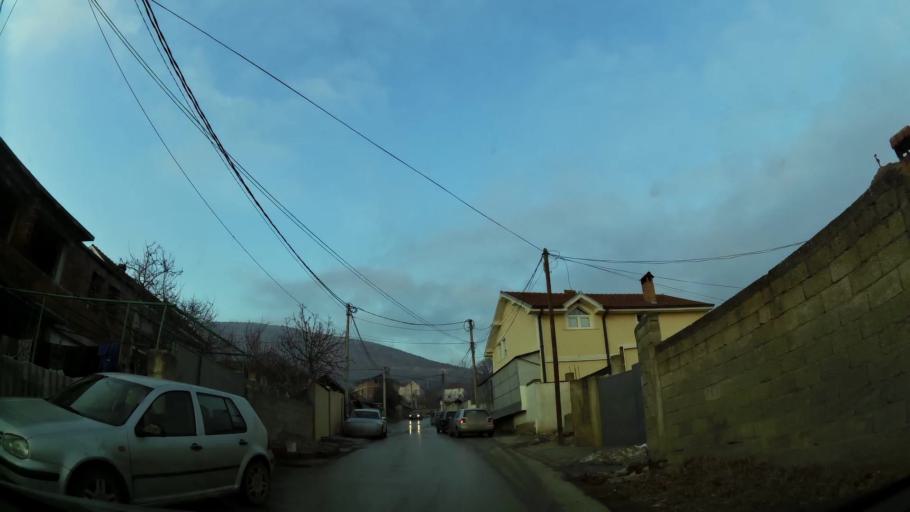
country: MK
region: Aracinovo
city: Arachinovo
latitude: 42.0321
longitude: 21.5658
